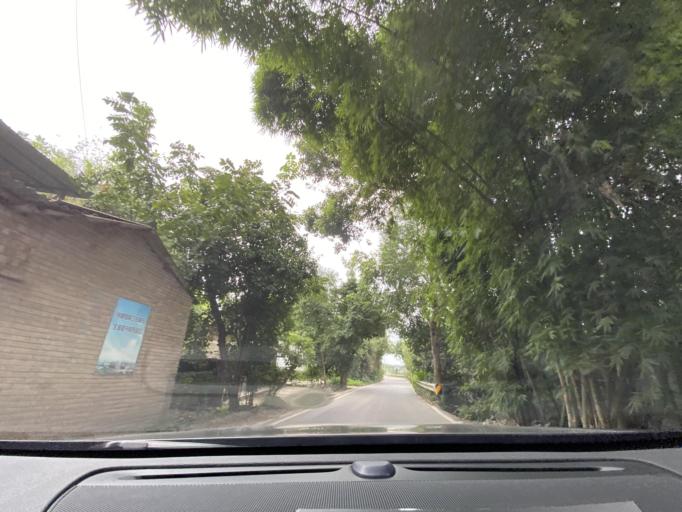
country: CN
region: Sichuan
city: Jiancheng
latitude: 30.4352
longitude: 104.5266
